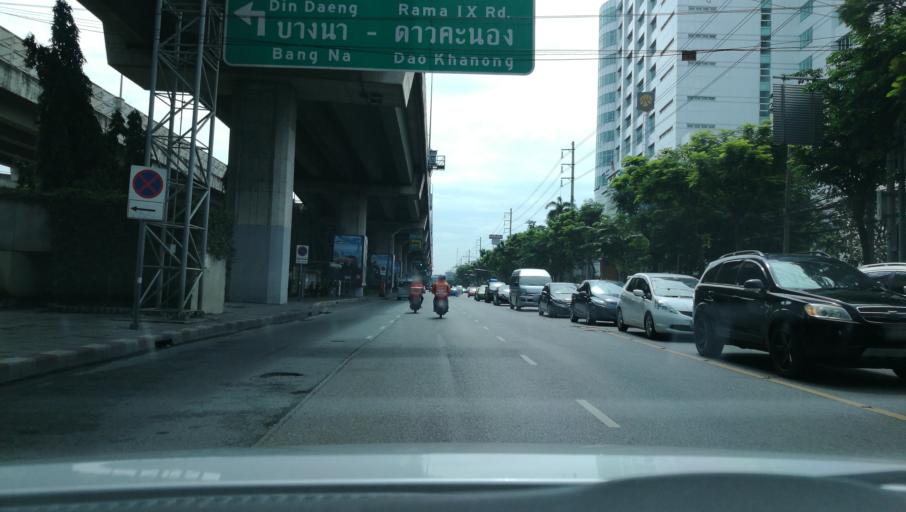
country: TH
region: Bangkok
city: Phaya Thai
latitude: 13.7813
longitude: 100.5337
